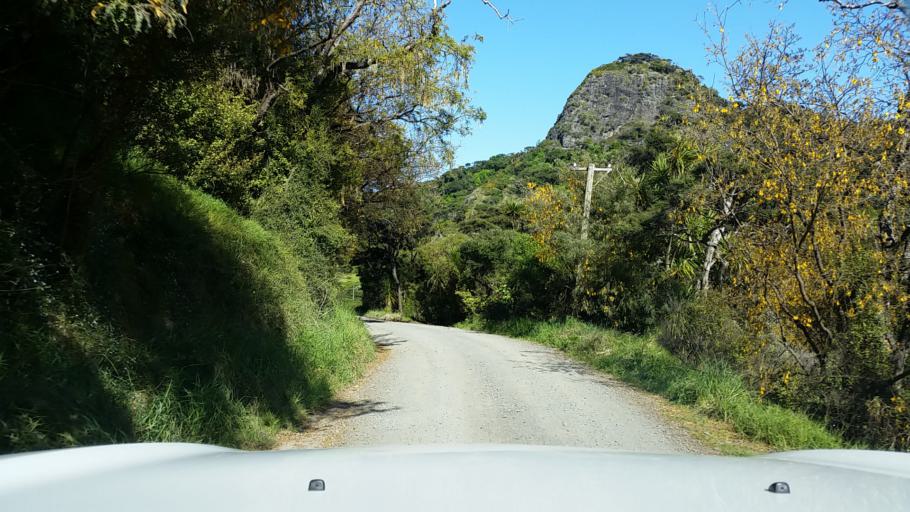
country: NZ
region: Auckland
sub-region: Auckland
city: Titirangi
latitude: -37.0373
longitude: 174.5129
